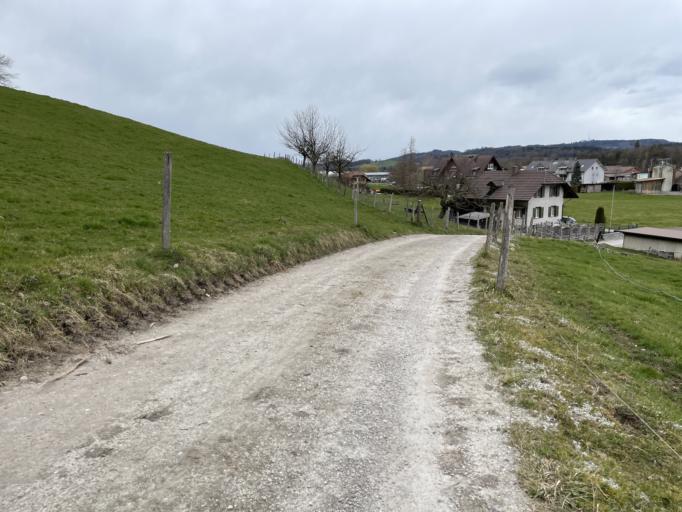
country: CH
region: Bern
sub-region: Bern-Mittelland District
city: Rubigen
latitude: 46.8852
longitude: 7.5259
